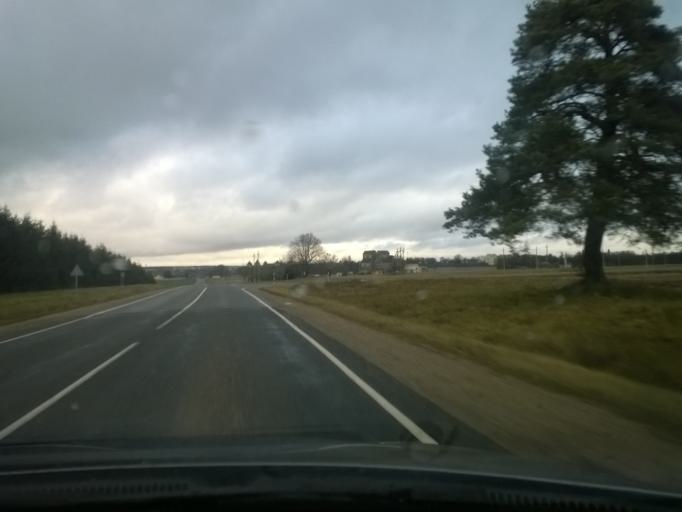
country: BY
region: Grodnenskaya
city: Mir
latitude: 53.4410
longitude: 26.4781
